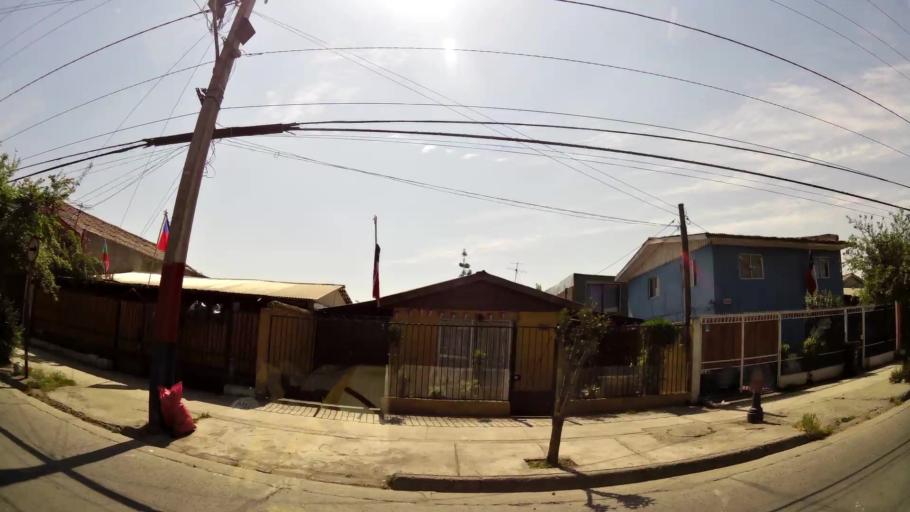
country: CL
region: Santiago Metropolitan
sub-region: Provincia de Santiago
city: La Pintana
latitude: -33.5463
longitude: -70.6424
